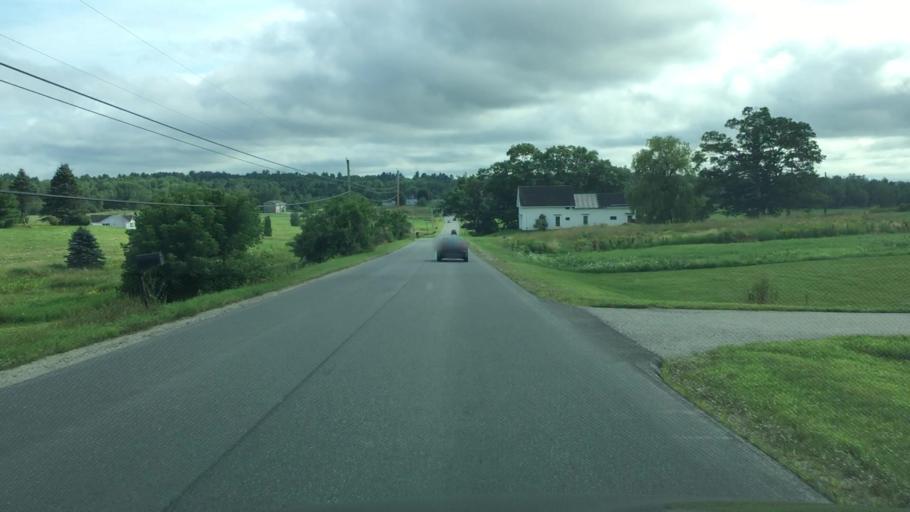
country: US
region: Maine
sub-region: Waldo County
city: Winterport
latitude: 44.6773
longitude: -68.8678
